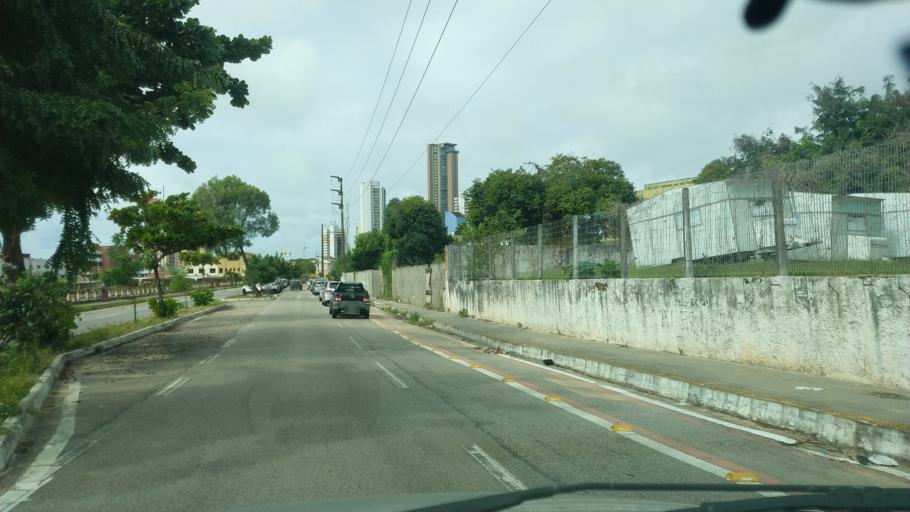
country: BR
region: Rio Grande do Norte
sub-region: Natal
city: Natal
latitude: -5.7815
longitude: -35.2080
